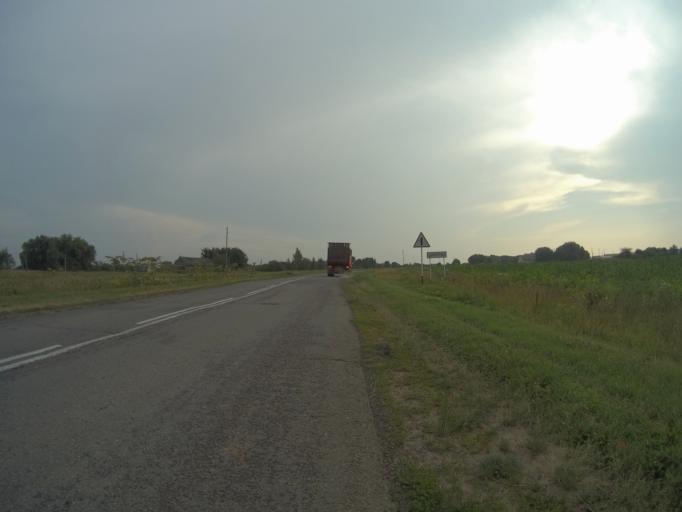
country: RU
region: Ivanovo
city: Gavrilov Posad
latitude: 56.3455
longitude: 40.2009
